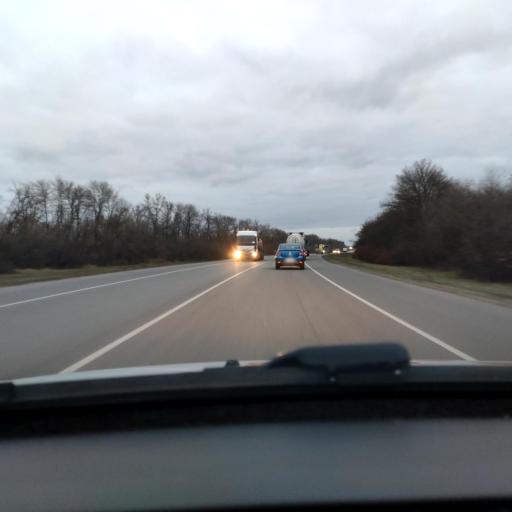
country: RU
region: Lipetsk
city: Borinskoye
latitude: 52.4552
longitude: 39.3029
